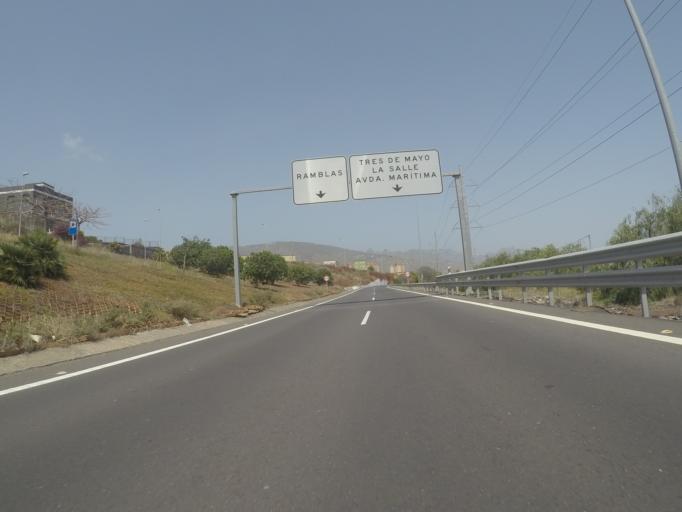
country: ES
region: Canary Islands
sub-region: Provincia de Santa Cruz de Tenerife
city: Santa Cruz de Tenerife
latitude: 28.4522
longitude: -16.2713
